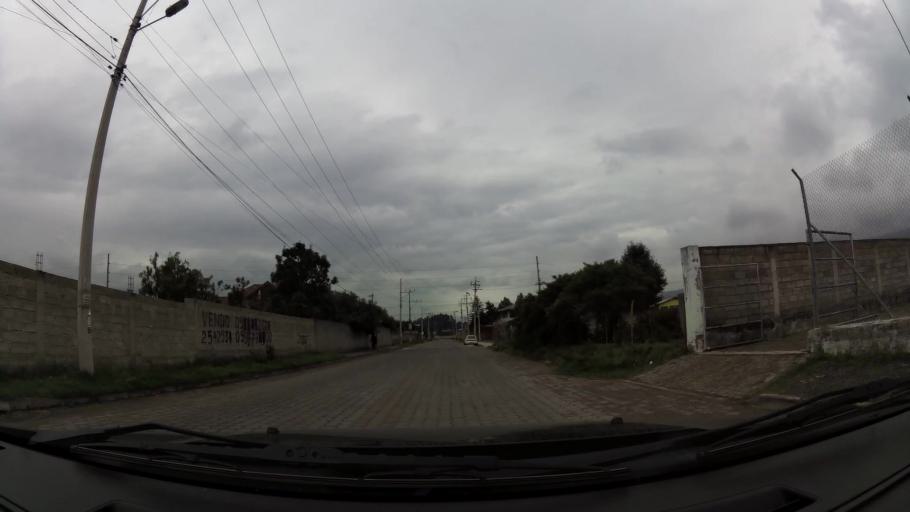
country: EC
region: Pichincha
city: Sangolqui
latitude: -0.3419
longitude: -78.4666
